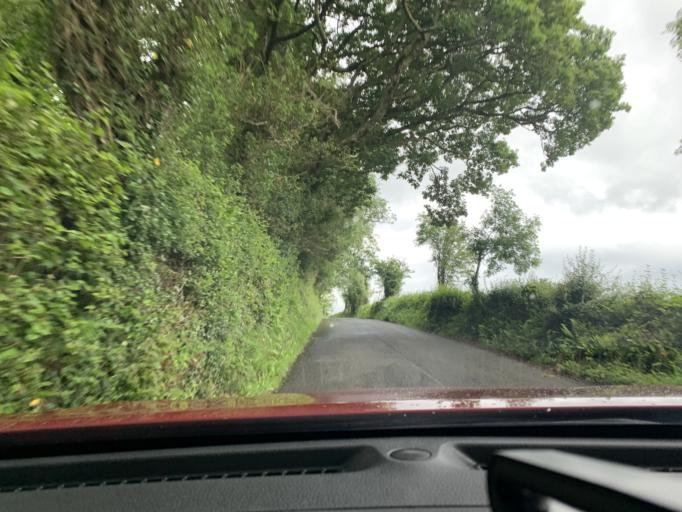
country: IE
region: Connaught
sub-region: County Leitrim
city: Manorhamilton
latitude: 54.3109
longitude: -8.1914
